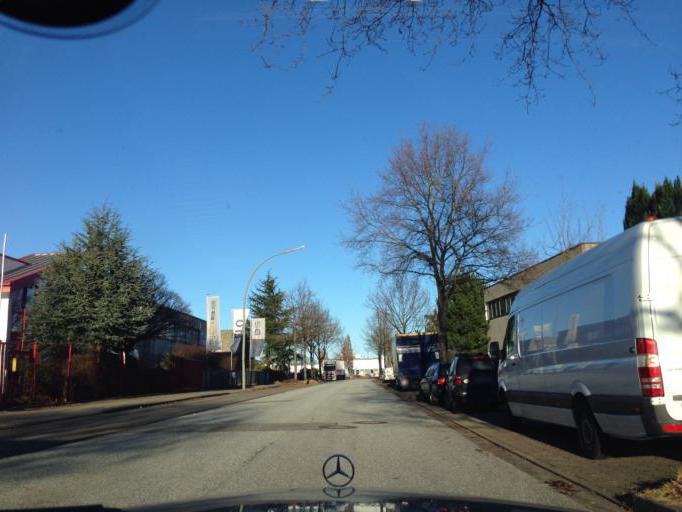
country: DE
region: Hamburg
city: Farmsen-Berne
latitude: 53.6022
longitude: 10.1130
